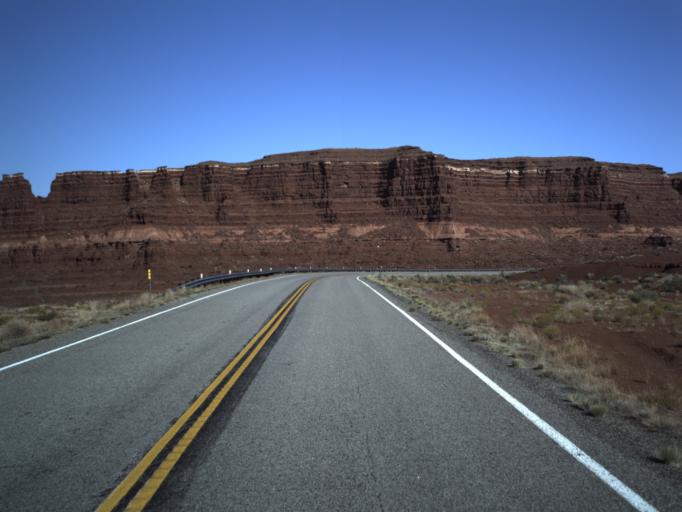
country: US
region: Utah
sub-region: San Juan County
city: Blanding
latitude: 37.8565
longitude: -110.3538
